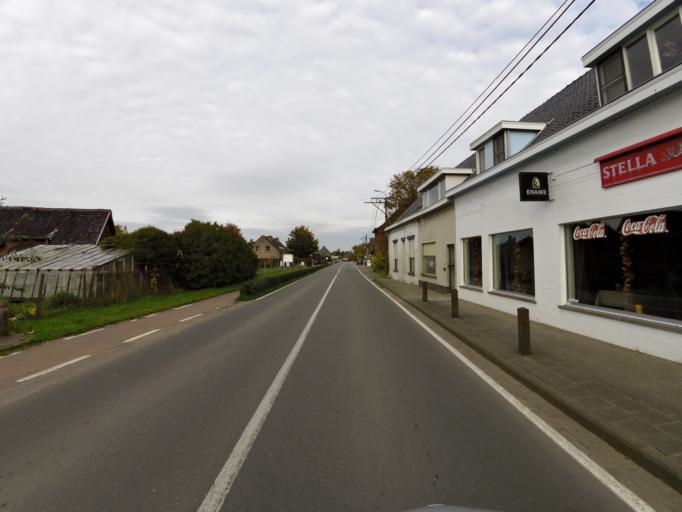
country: BE
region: Flanders
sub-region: Provincie West-Vlaanderen
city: Torhout
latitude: 51.0859
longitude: 3.0989
